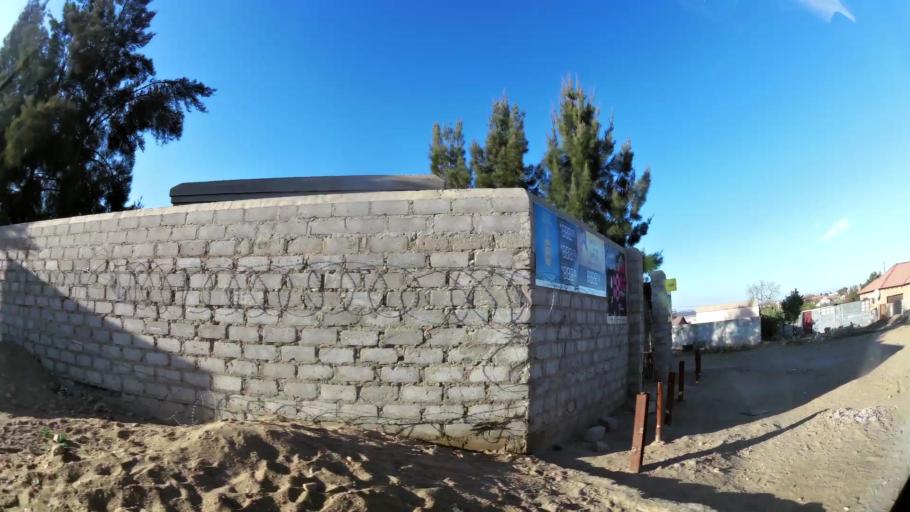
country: ZA
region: Limpopo
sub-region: Capricorn District Municipality
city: Polokwane
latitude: -23.8402
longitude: 29.3612
